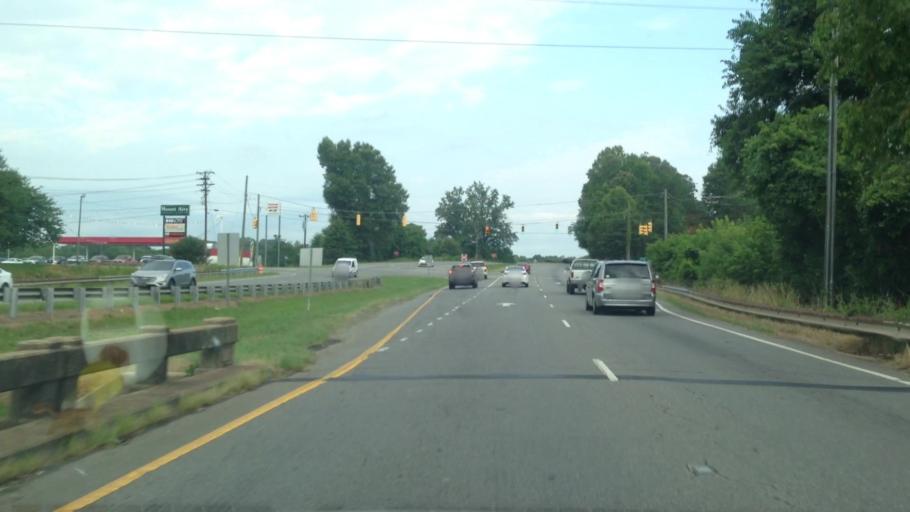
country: US
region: North Carolina
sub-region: Surry County
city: Mount Airy
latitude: 36.4801
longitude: -80.6005
